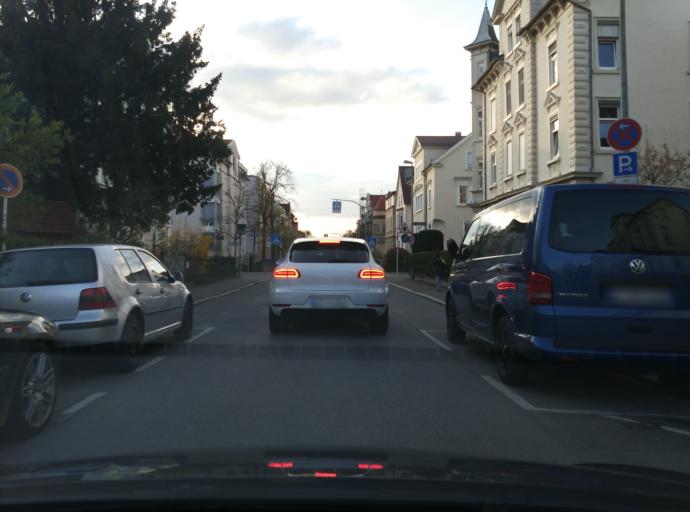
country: DE
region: Baden-Wuerttemberg
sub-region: Tuebingen Region
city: Reutlingen
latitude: 48.4947
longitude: 9.2170
